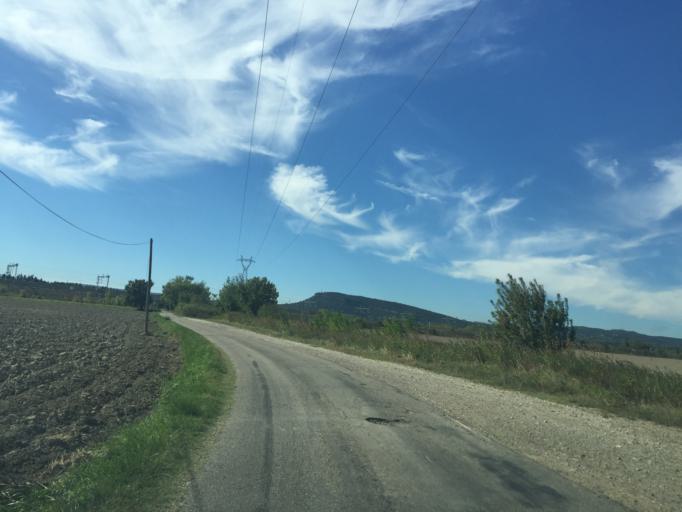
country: FR
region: Provence-Alpes-Cote d'Azur
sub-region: Departement du Vaucluse
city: Piolenc
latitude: 44.1568
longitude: 4.7489
